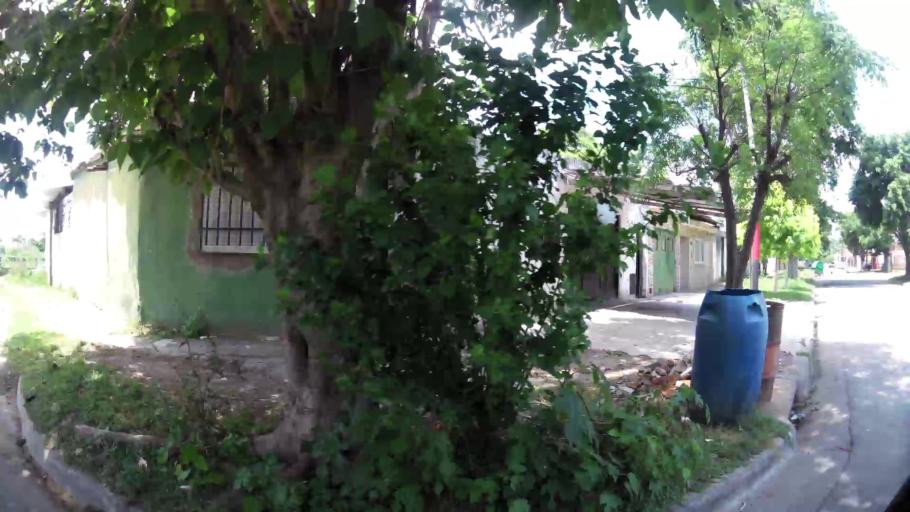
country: AR
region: Santa Fe
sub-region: Departamento de Rosario
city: Rosario
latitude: -32.9716
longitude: -60.6255
